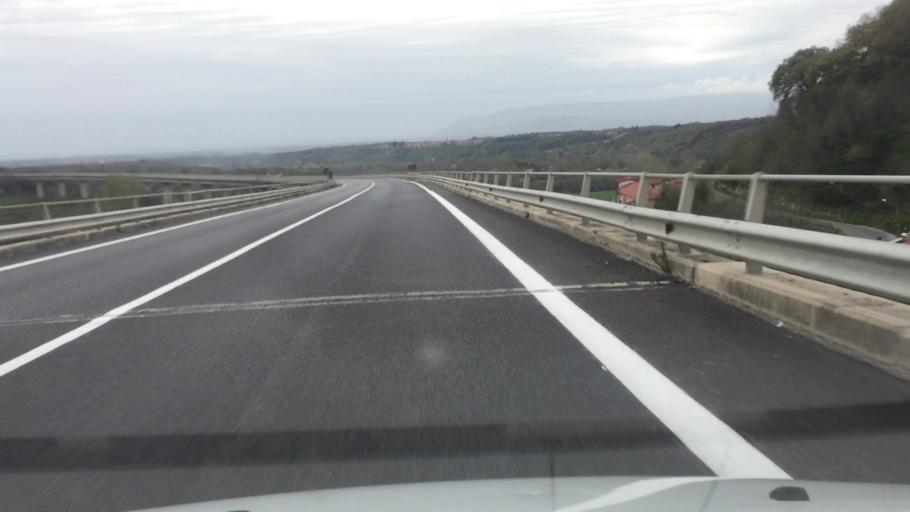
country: IT
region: Calabria
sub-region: Provincia di Reggio Calabria
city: Anoia Superiore
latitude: 38.4193
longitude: 16.1017
